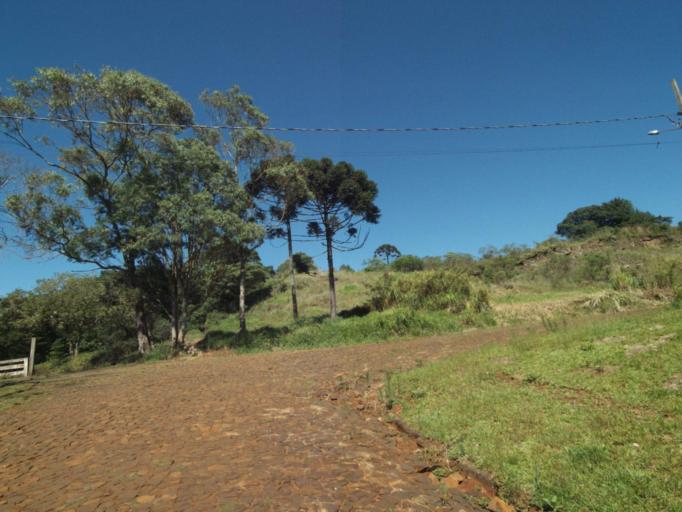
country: BR
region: Santa Catarina
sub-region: Sao Lourenco Do Oeste
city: Sao Lourenco dOeste
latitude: -26.2714
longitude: -52.7839
